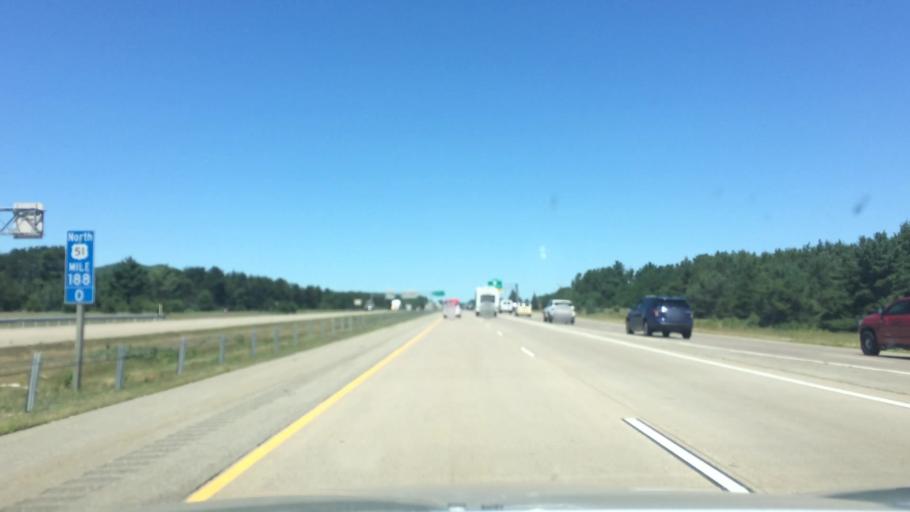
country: US
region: Wisconsin
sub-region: Marathon County
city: Rothschild
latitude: 44.8999
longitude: -89.6422
